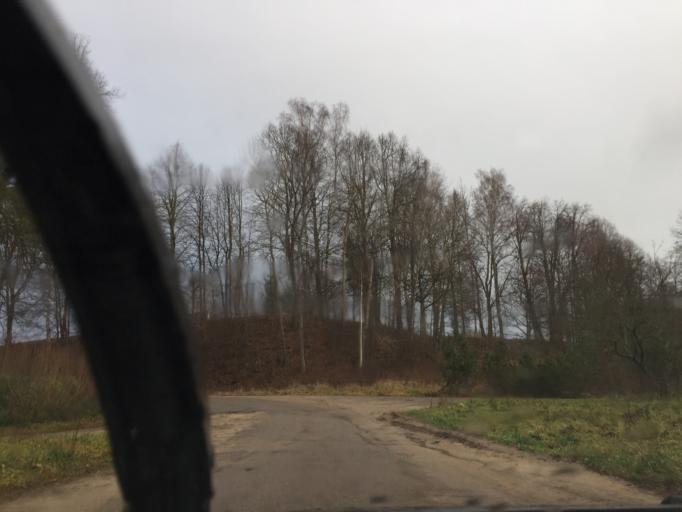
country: LV
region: Valmieras Rajons
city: Valmiera
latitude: 57.5433
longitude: 25.4573
